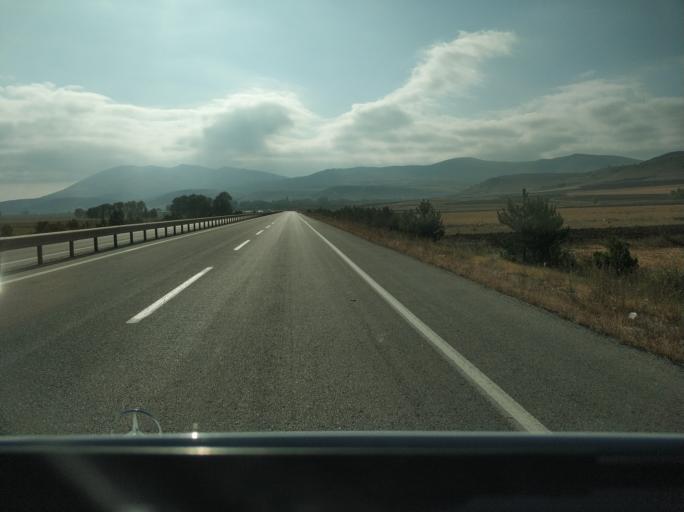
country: TR
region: Sivas
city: Yildizeli
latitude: 39.8497
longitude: 36.5118
